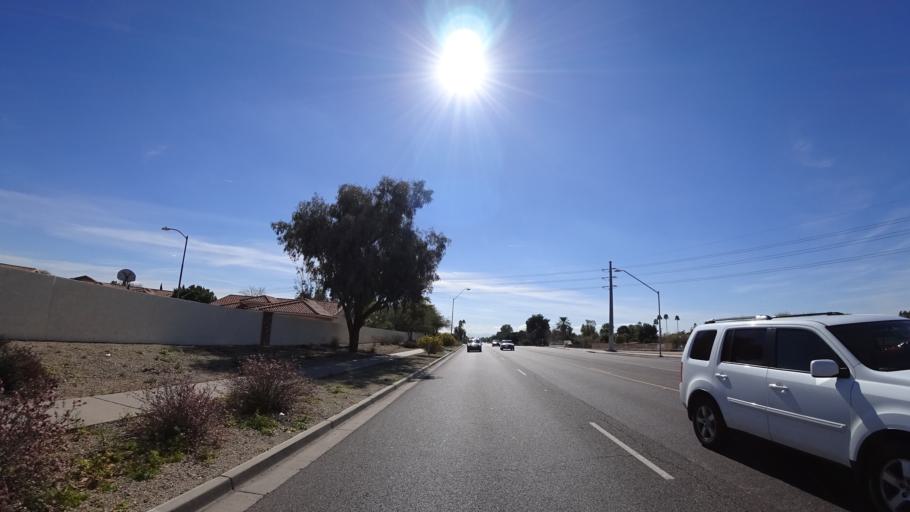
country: US
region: Arizona
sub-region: Maricopa County
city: Peoria
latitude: 33.6192
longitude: -112.2024
